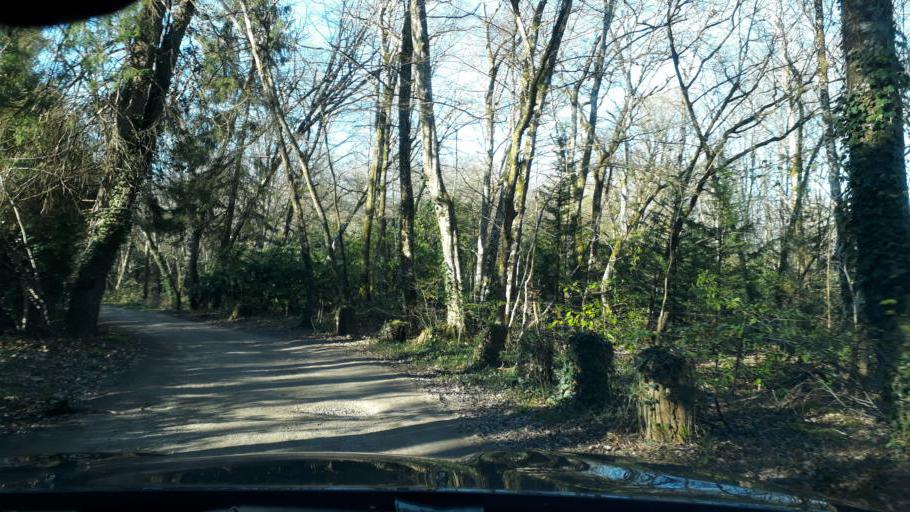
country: FR
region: Centre
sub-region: Departement du Loiret
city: Jouy-le-Potier
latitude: 47.7056
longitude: 1.8346
